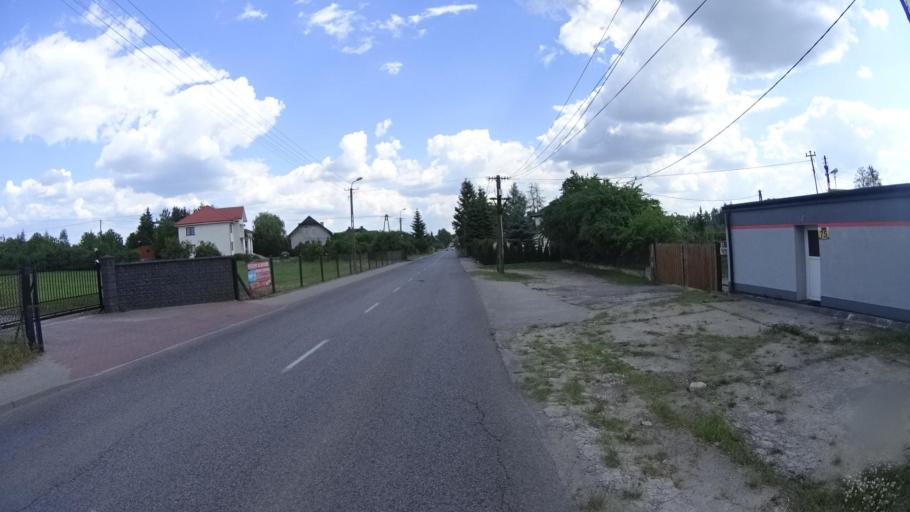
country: PL
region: Masovian Voivodeship
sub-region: Powiat piaseczynski
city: Tarczyn
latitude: 51.9873
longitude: 20.8264
